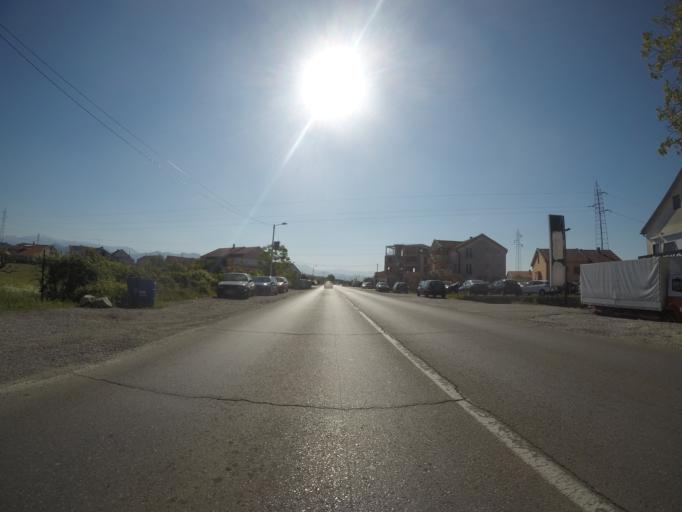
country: ME
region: Podgorica
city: Podgorica
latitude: 42.4386
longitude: 19.2237
